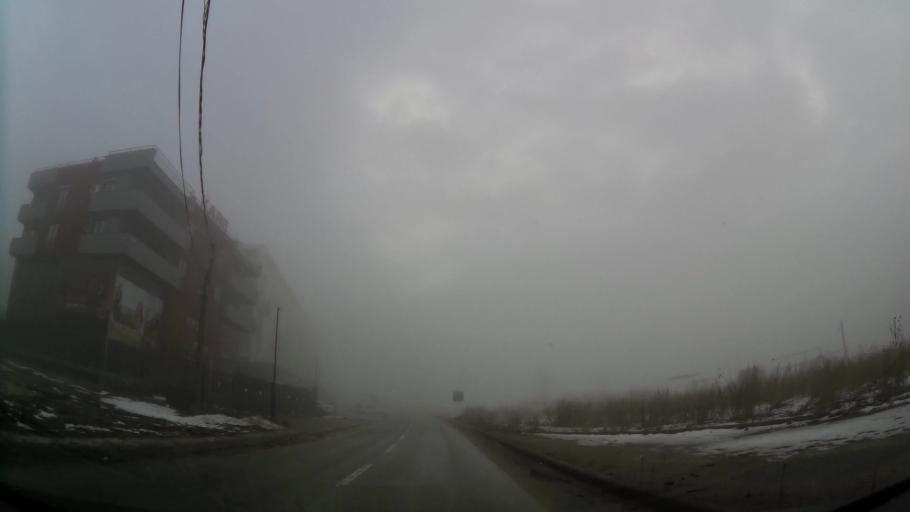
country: XK
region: Pristina
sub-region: Komuna e Prishtines
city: Pristina
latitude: 42.6582
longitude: 21.1397
